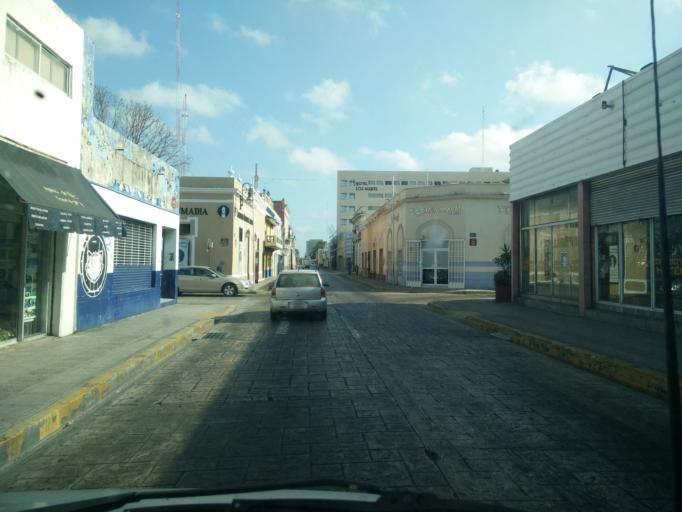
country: MX
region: Yucatan
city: Merida
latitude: 20.9728
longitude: -89.6221
